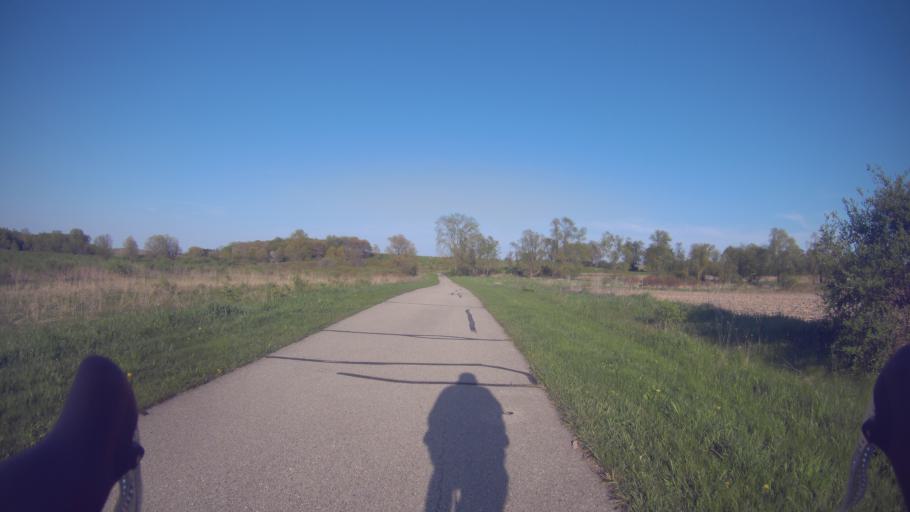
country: US
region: Wisconsin
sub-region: Dane County
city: Monona
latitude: 43.0229
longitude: -89.3578
